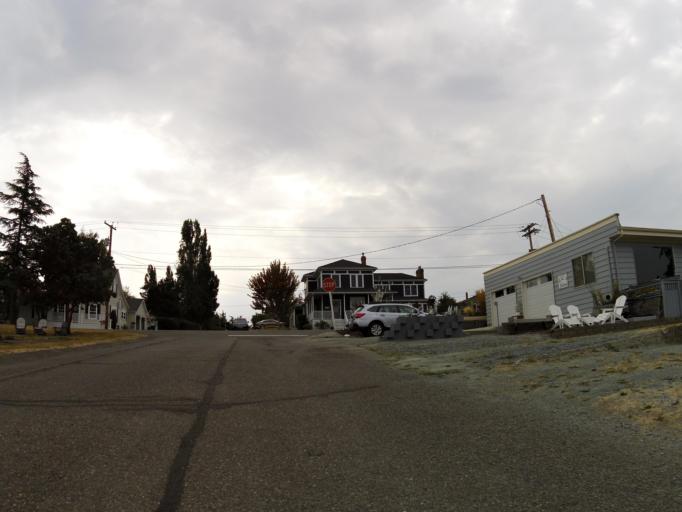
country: US
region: Washington
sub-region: Island County
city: Coupeville
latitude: 48.2204
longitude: -122.6851
